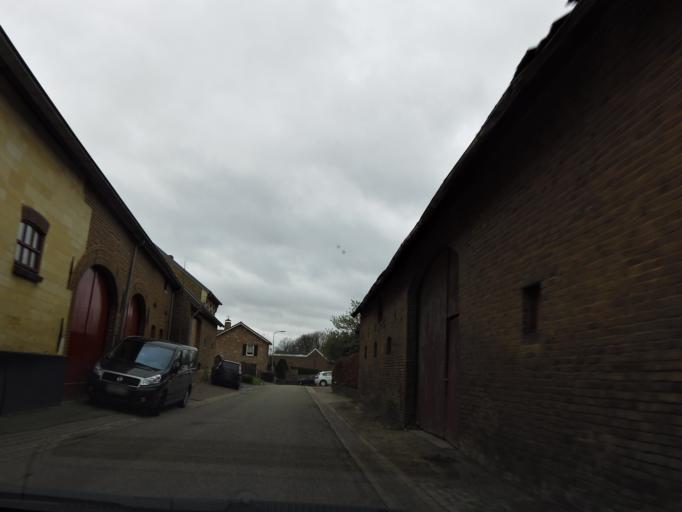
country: NL
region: Limburg
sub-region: Eijsden-Margraten
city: Margraten
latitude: 50.8050
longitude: 5.8035
